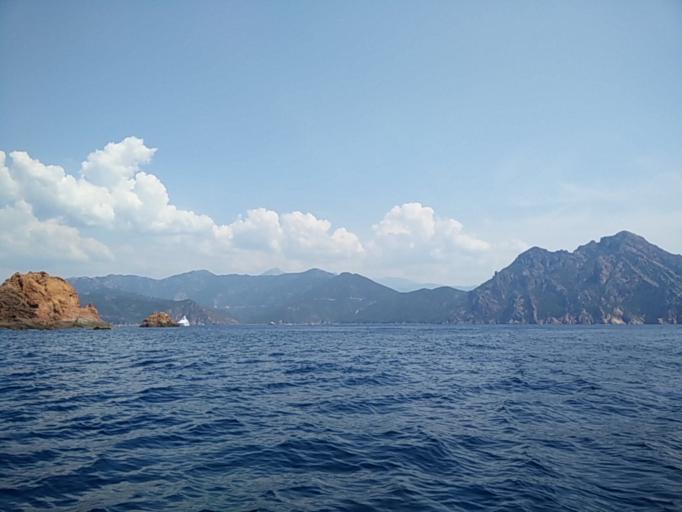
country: FR
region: Corsica
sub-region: Departement de la Corse-du-Sud
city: Cargese
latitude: 42.3368
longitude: 8.5687
